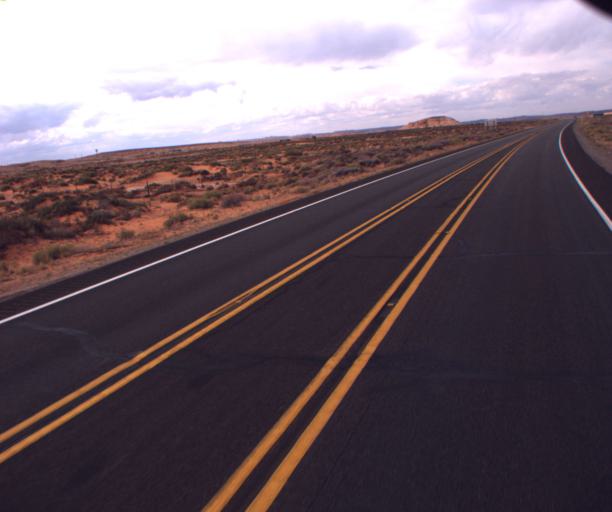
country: US
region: Arizona
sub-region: Apache County
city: Many Farms
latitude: 36.9257
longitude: -109.6158
